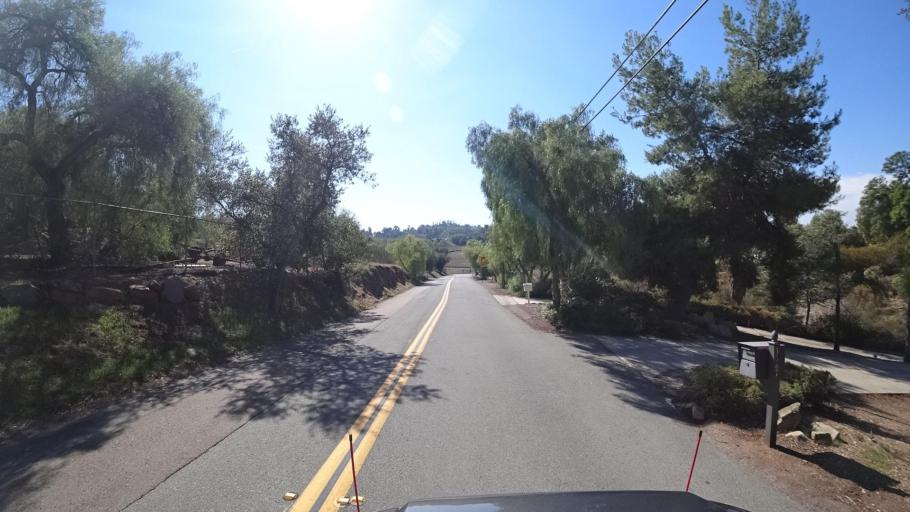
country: US
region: California
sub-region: San Diego County
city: Rancho San Diego
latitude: 32.7762
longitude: -116.9368
